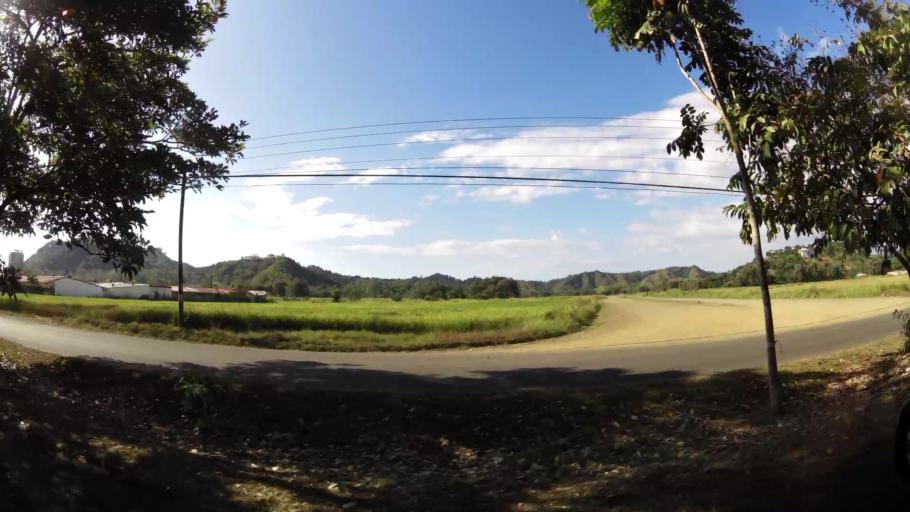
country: CR
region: Puntarenas
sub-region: Canton de Garabito
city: Jaco
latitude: 9.6254
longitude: -84.6347
